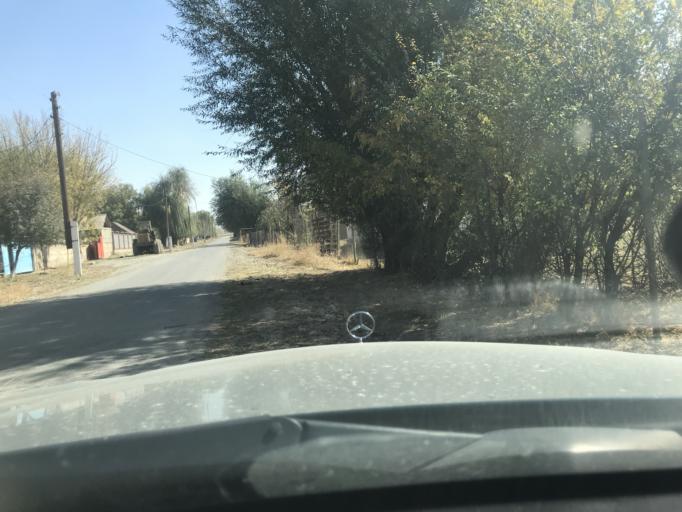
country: KZ
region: Ongtustik Qazaqstan
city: Sastobe
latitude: 42.5445
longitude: 69.9342
